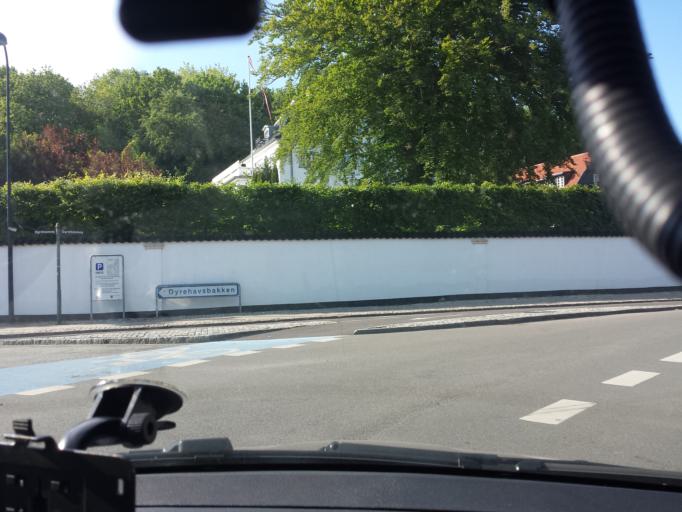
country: DK
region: Capital Region
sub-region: Gentofte Kommune
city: Charlottenlund
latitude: 55.7748
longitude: 12.5840
